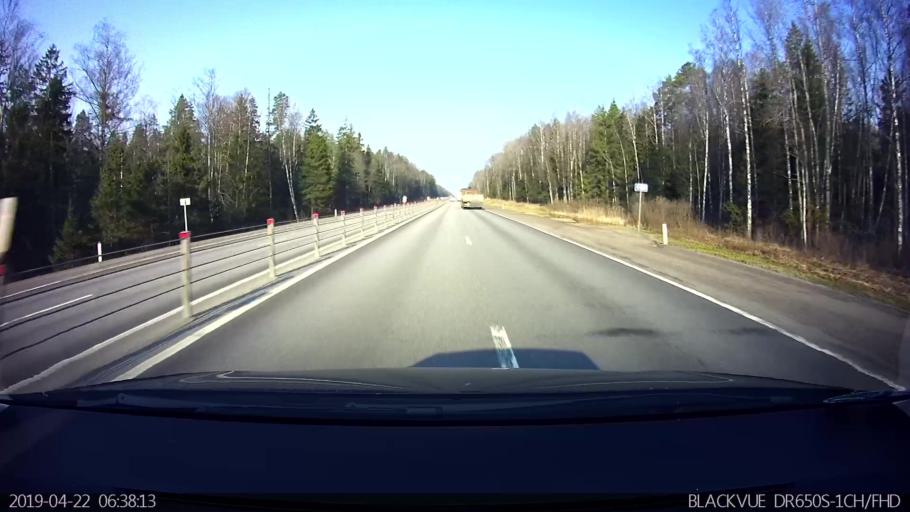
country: RU
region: Moskovskaya
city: Uvarovka
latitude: 55.4915
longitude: 35.3811
